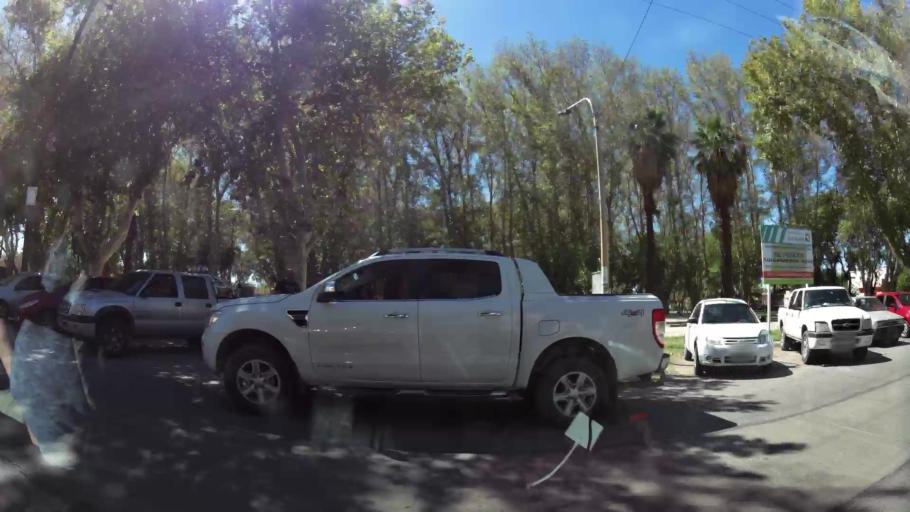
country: AR
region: San Juan
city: Villa Krause
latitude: -31.5517
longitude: -68.5228
